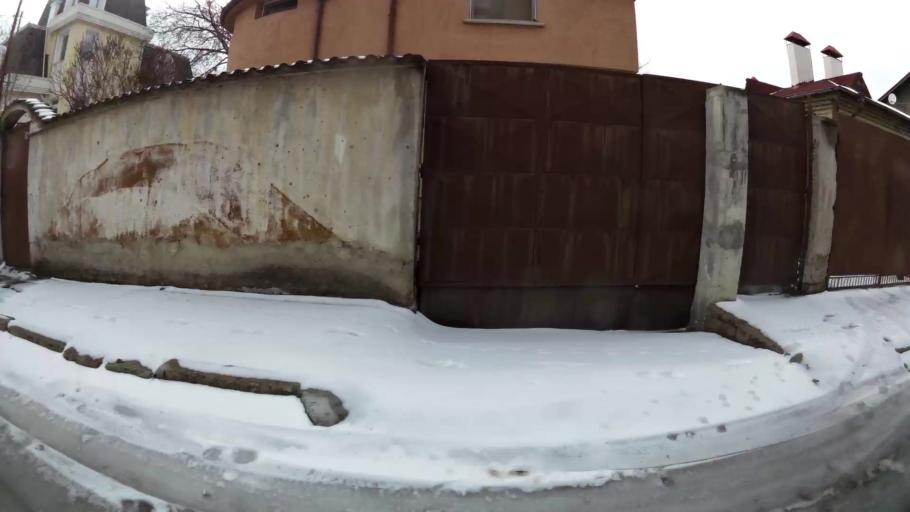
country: BG
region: Sofia-Capital
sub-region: Stolichna Obshtina
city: Sofia
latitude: 42.7004
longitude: 23.3792
